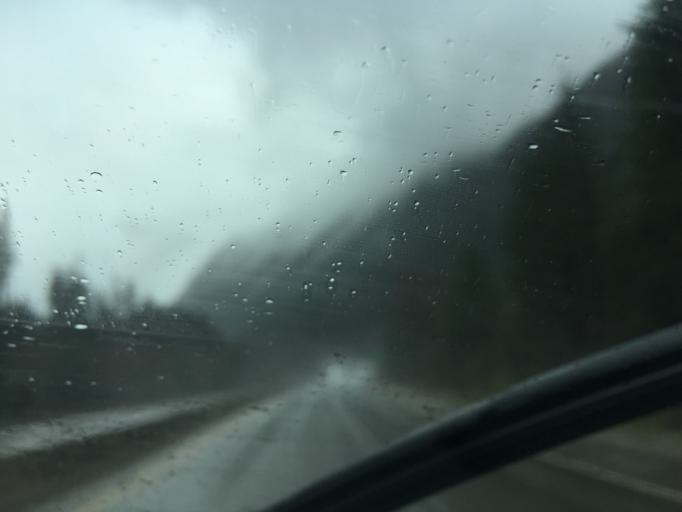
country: CA
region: British Columbia
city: Hope
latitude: 49.5270
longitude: -121.2059
